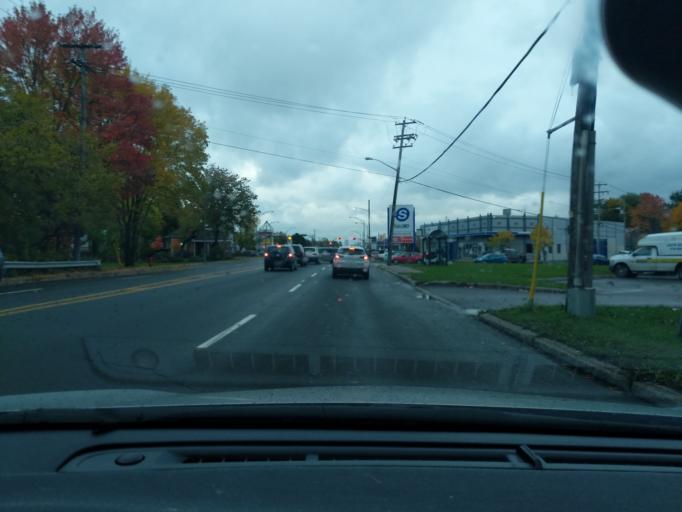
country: CA
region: Quebec
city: L'Ancienne-Lorette
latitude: 46.8060
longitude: -71.3186
